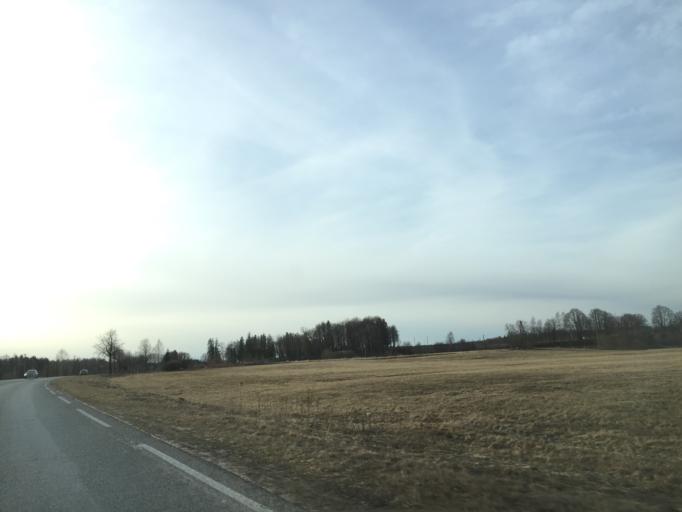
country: LV
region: Krimulda
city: Ragana
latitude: 57.1643
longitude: 24.7547
